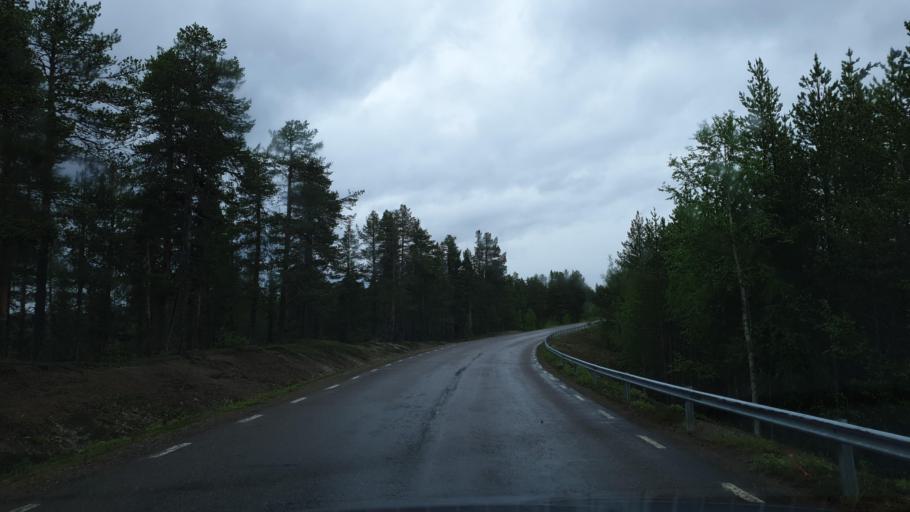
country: SE
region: Norrbotten
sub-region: Kiruna Kommun
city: Kiruna
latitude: 67.8810
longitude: 20.9975
